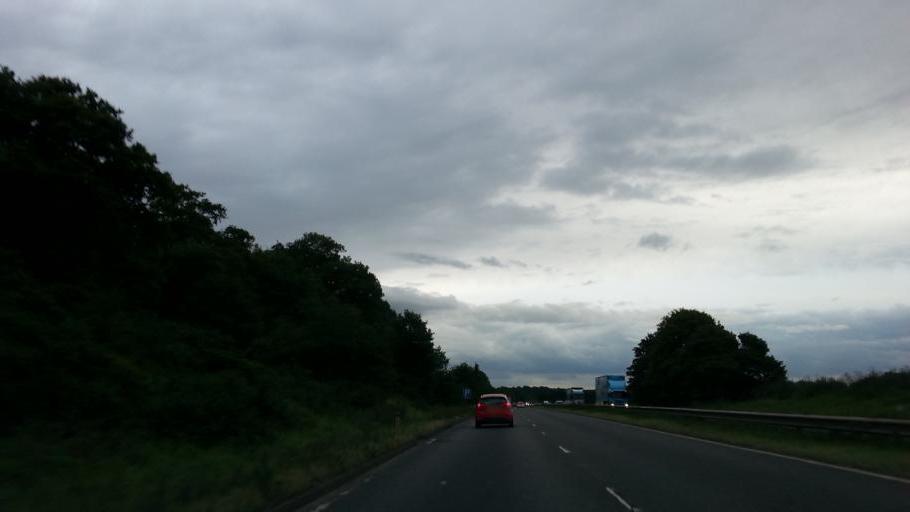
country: GB
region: England
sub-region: Nottinghamshire
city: Babworth
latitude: 53.3343
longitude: -1.0281
